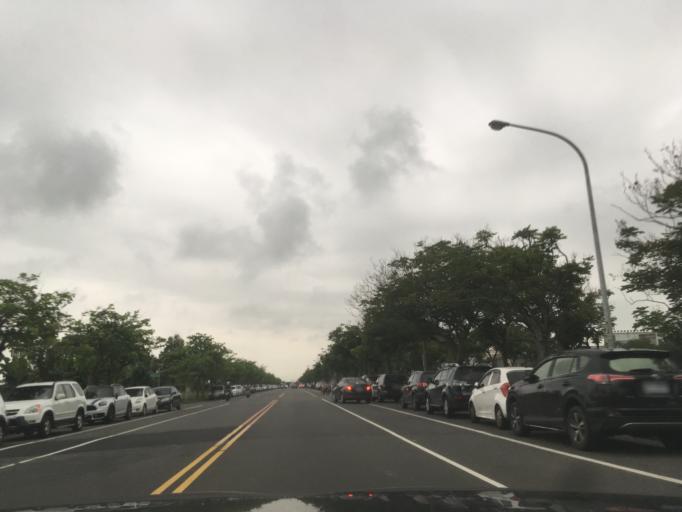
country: TW
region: Taiwan
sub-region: Yilan
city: Yilan
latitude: 24.7383
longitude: 121.7563
